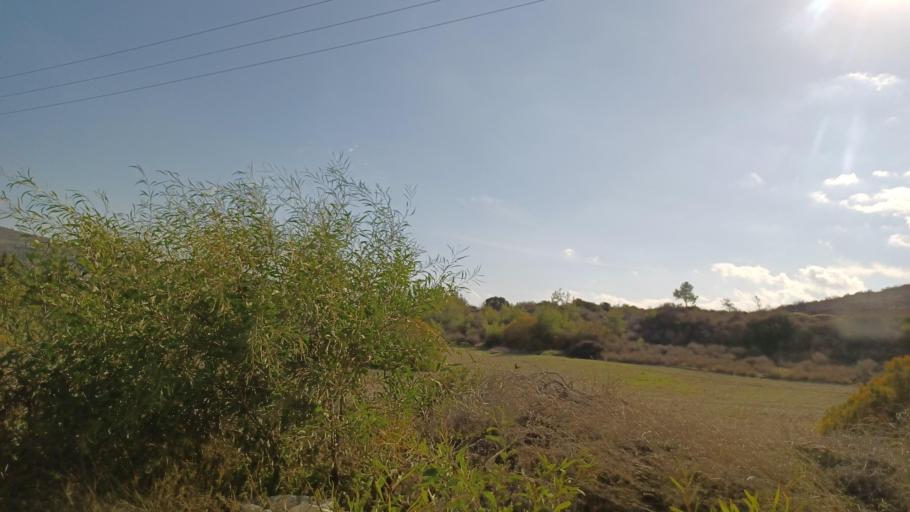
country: CY
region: Limassol
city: Pyrgos
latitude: 34.7209
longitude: 33.1924
